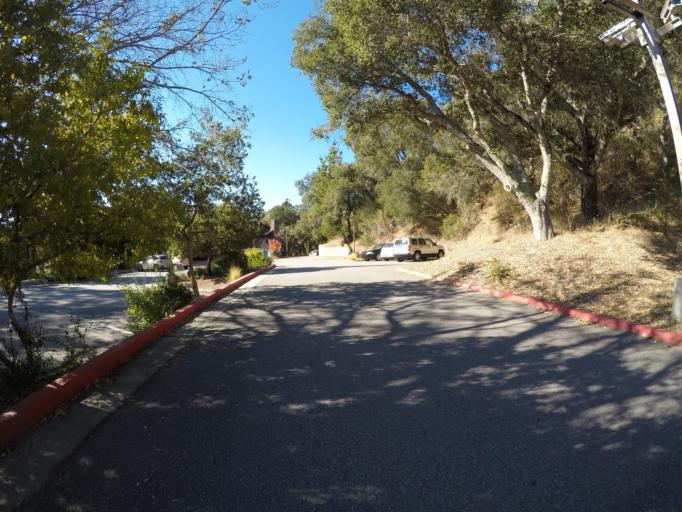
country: US
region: California
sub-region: Santa Cruz County
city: Scotts Valley
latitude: 37.0501
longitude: -122.0185
